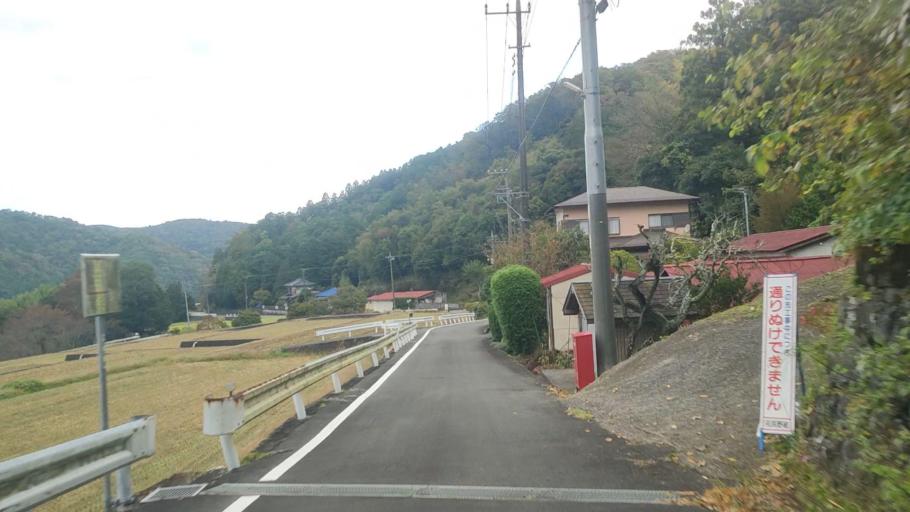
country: JP
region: Shizuoka
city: Ito
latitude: 34.9324
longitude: 139.0036
